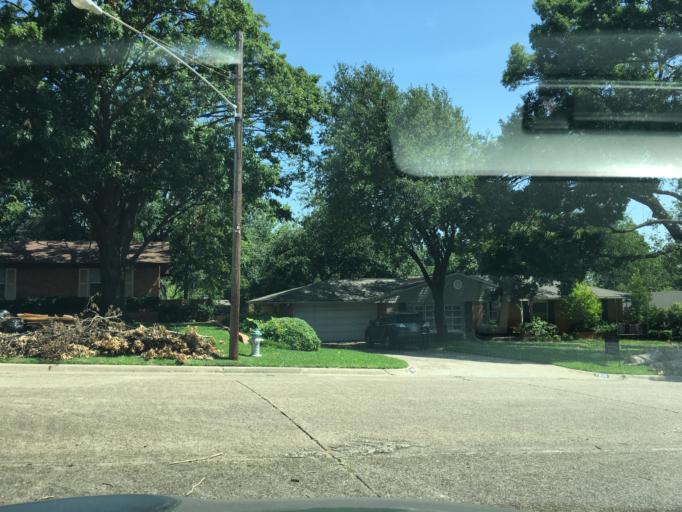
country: US
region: Texas
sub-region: Dallas County
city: University Park
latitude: 32.9030
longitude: -96.7743
